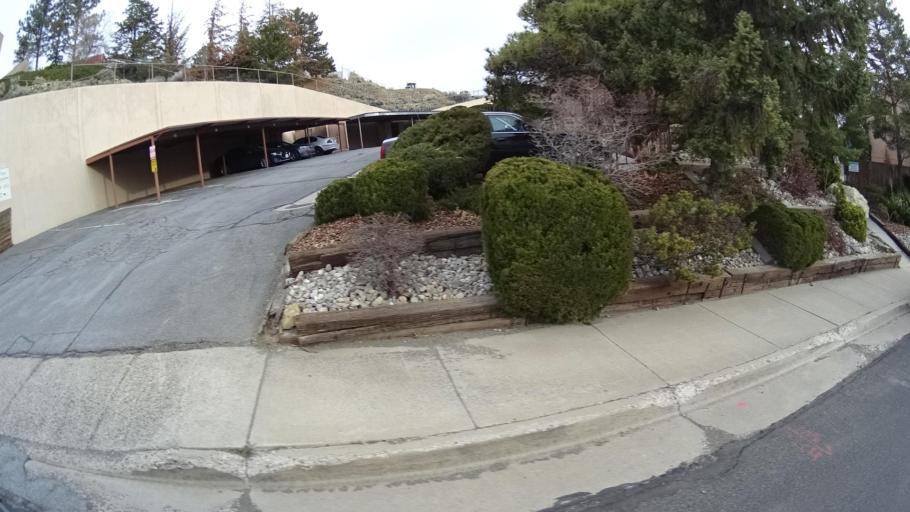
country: US
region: Nevada
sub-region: Washoe County
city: Reno
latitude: 39.5693
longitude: -119.8259
